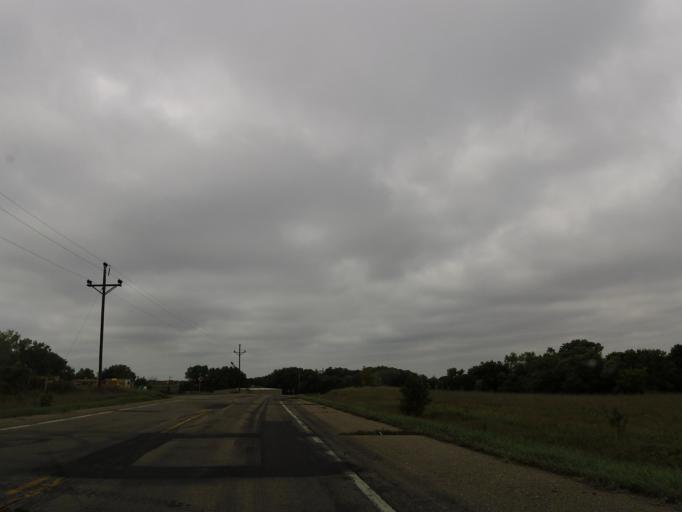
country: US
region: Minnesota
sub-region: Yellow Medicine County
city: Granite Falls
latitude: 44.8578
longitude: -95.6291
